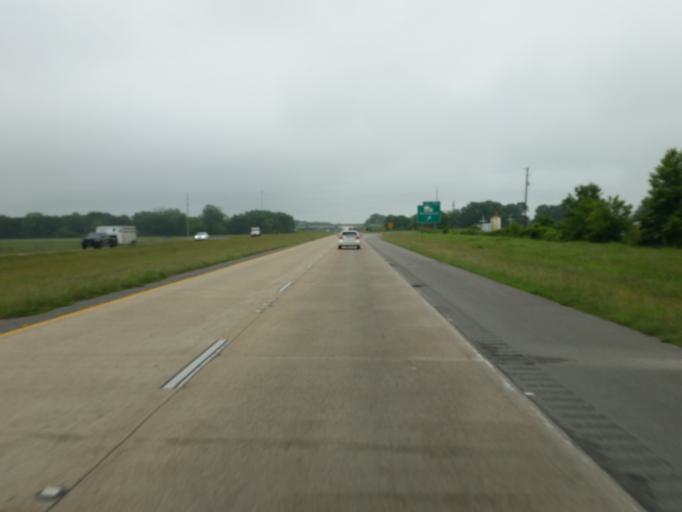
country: US
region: Louisiana
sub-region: Madison Parish
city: Tallulah
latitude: 32.3825
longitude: -91.1786
